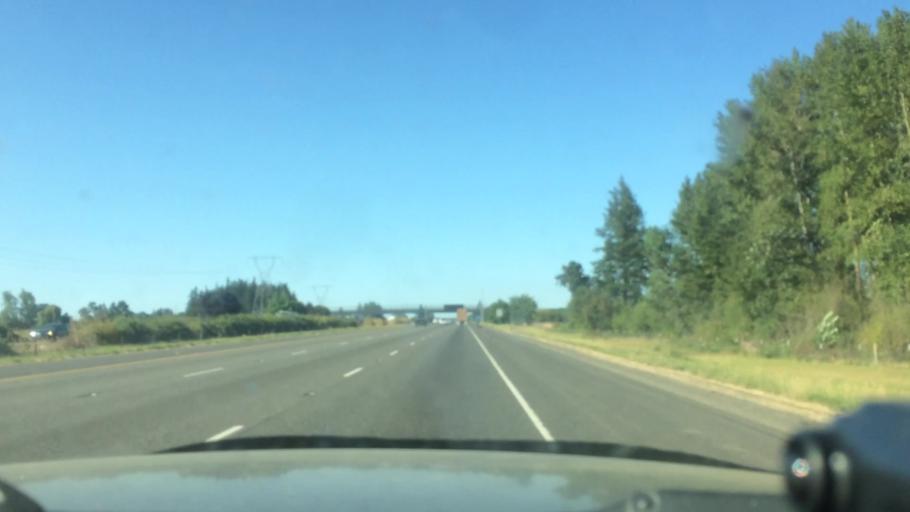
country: US
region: Oregon
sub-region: Marion County
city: Hayesville
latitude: 45.0245
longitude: -122.9860
